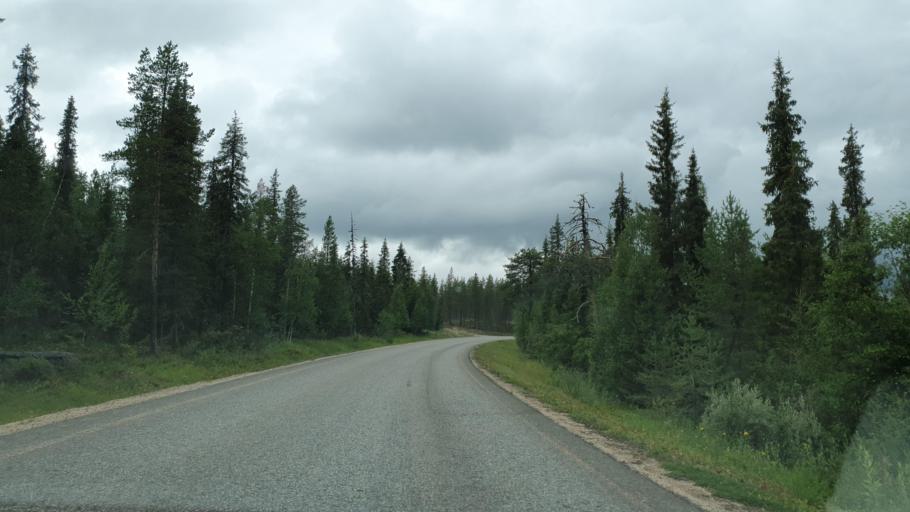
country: FI
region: Lapland
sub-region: Tunturi-Lappi
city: Kolari
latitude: 67.5071
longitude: 24.2250
